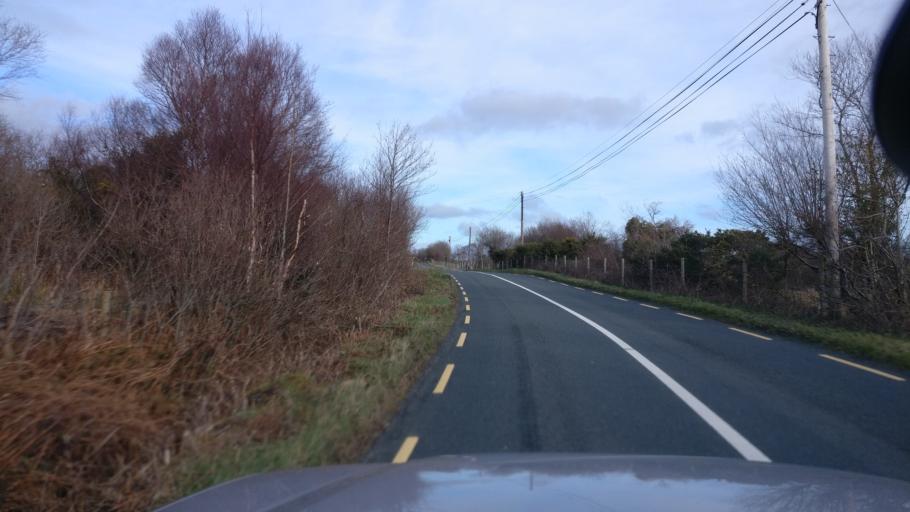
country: IE
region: Connaught
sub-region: County Galway
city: Oughterard
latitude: 53.5145
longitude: -9.4270
